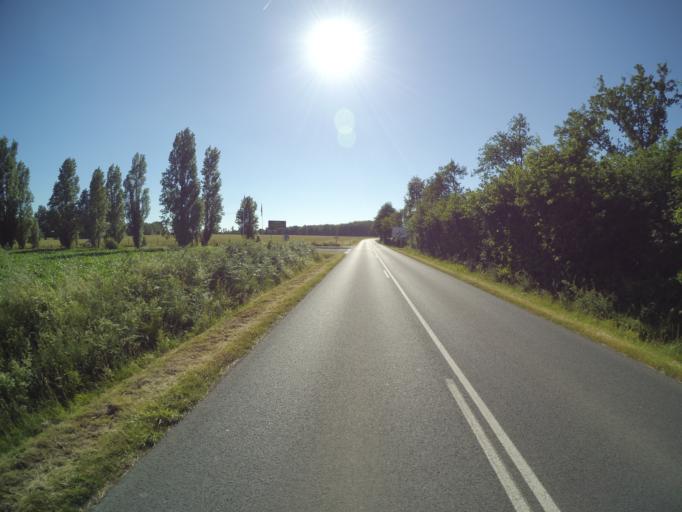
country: FR
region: Pays de la Loire
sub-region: Departement de la Vendee
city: La Guyonniere
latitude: 46.9581
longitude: -1.2458
